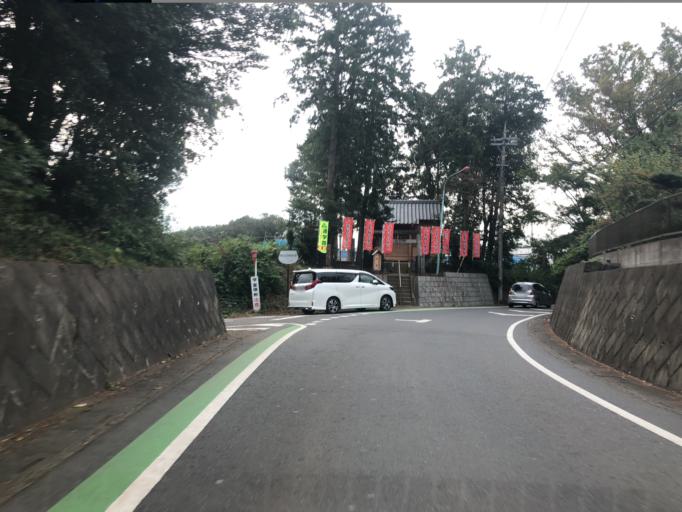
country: JP
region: Saitama
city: Fukiage-fujimi
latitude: 36.0558
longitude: 139.3970
